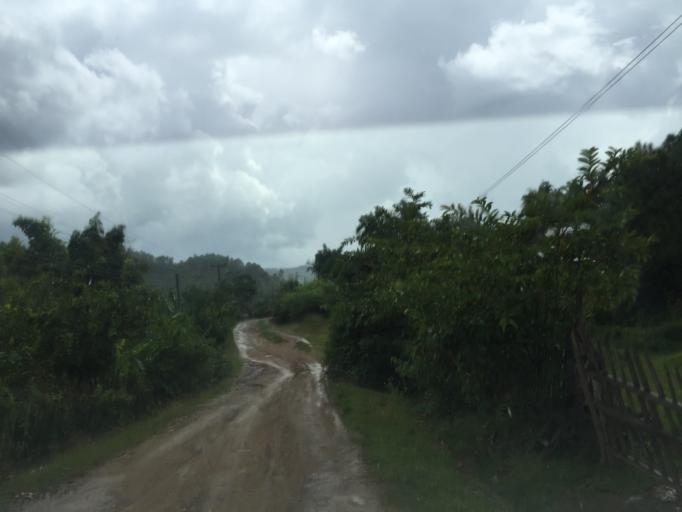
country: LA
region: Xiangkhoang
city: Muang Phonsavan
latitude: 19.3396
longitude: 103.5750
